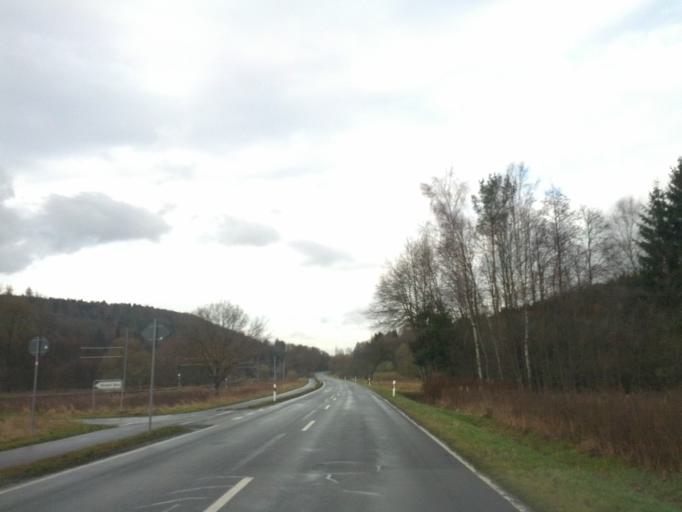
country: DE
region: Hesse
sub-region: Regierungsbezirk Kassel
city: Helsa
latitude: 51.2663
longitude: 9.6752
